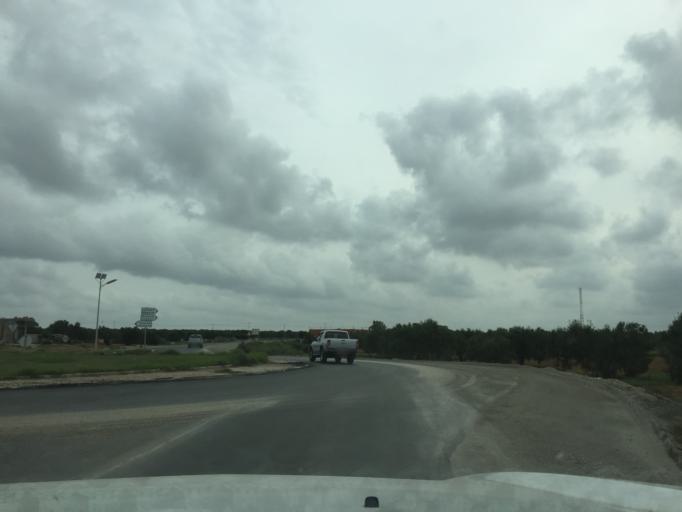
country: TN
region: Al Munastir
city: Manzil Kamil
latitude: 35.6488
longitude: 10.5905
